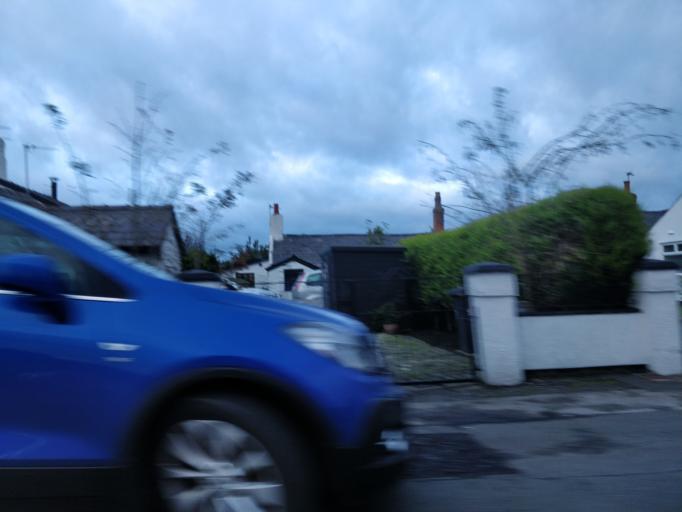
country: GB
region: England
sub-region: Sefton
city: Southport
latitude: 53.6666
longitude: -2.9775
